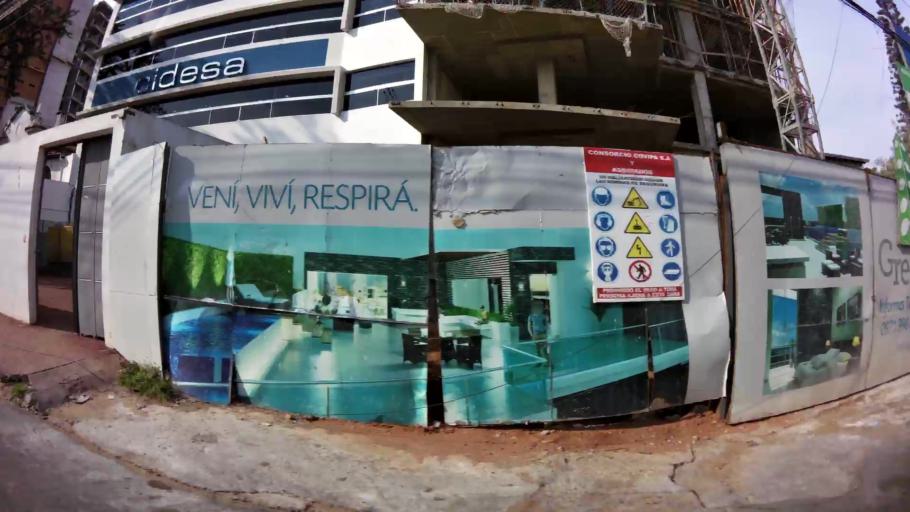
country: PY
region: Asuncion
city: Asuncion
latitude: -25.2861
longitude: -57.6173
